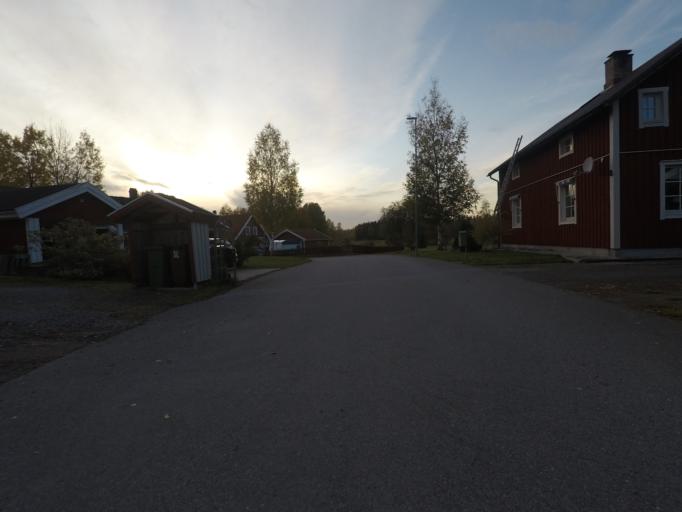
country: SE
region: OErebro
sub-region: Karlskoga Kommun
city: Karlskoga
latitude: 59.3008
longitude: 14.4872
